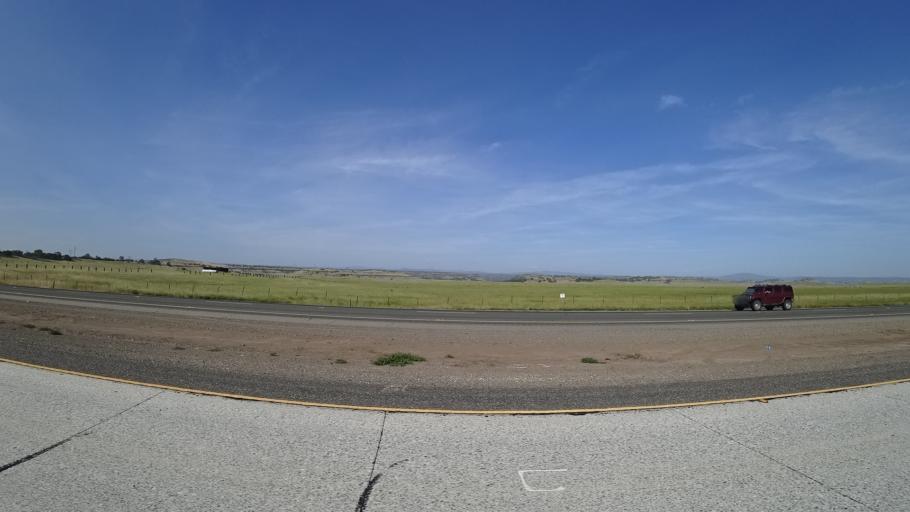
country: US
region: California
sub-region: Butte County
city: Durham
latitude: 39.6552
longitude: -121.7312
